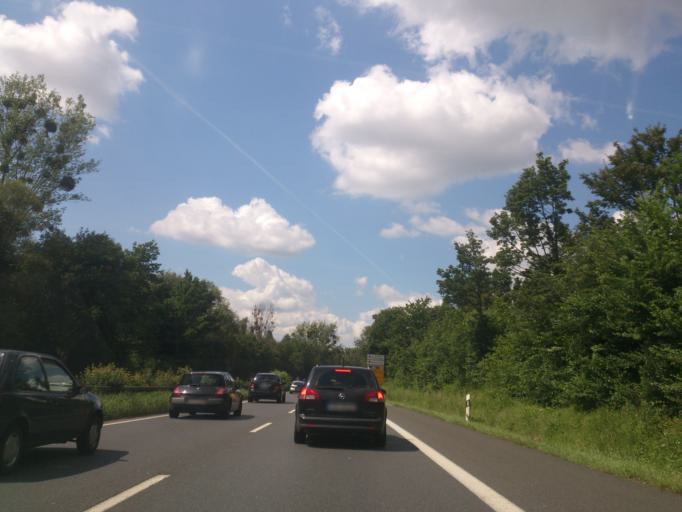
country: DE
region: Lower Saxony
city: Auf der Horst
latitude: 52.4058
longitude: 9.6571
